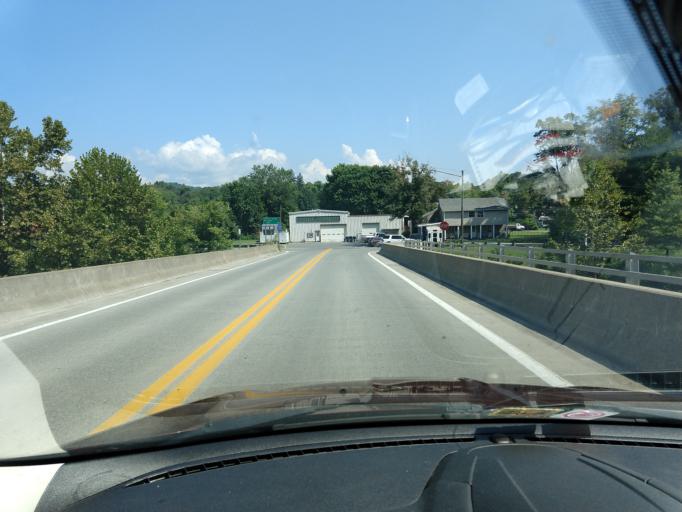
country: US
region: West Virginia
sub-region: Greenbrier County
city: Alderson
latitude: 37.7269
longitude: -80.6496
